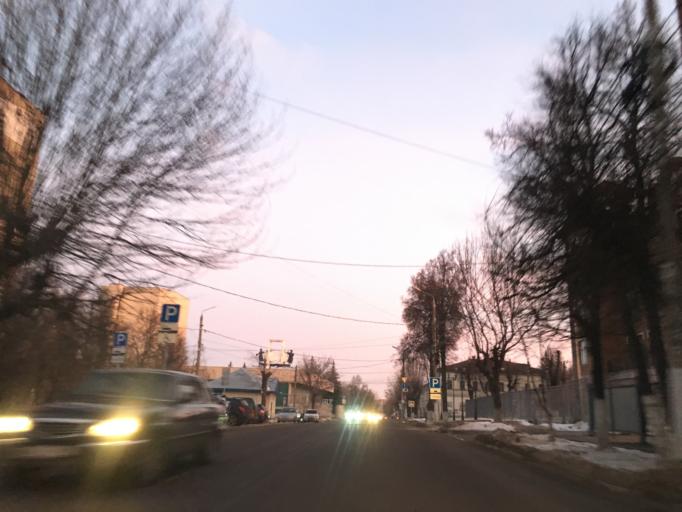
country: RU
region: Tula
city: Tula
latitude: 54.1889
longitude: 37.6073
